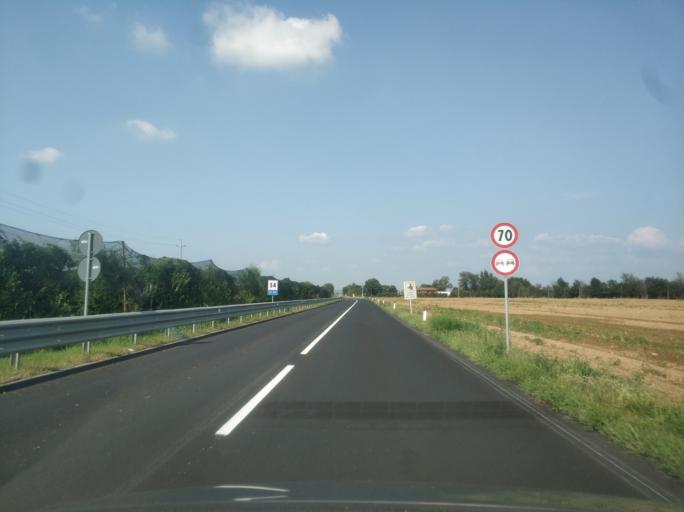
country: IT
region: Piedmont
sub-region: Provincia di Cuneo
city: Cervere
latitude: 44.6115
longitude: 7.7719
